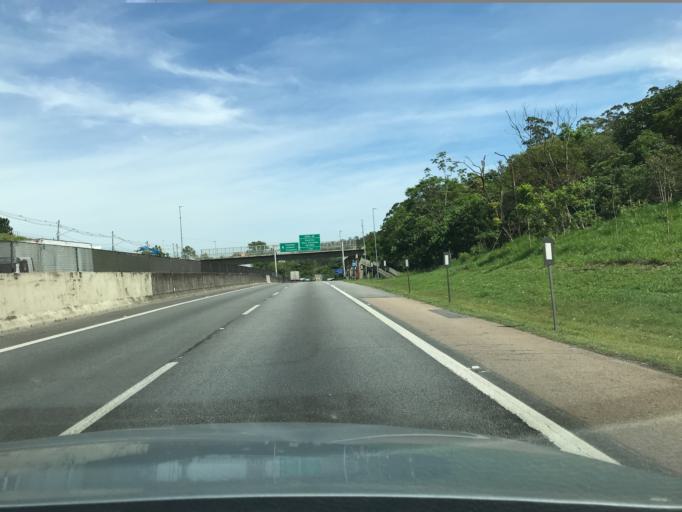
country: BR
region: Sao Paulo
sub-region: Caieiras
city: Caieiras
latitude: -23.4149
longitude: -46.8052
